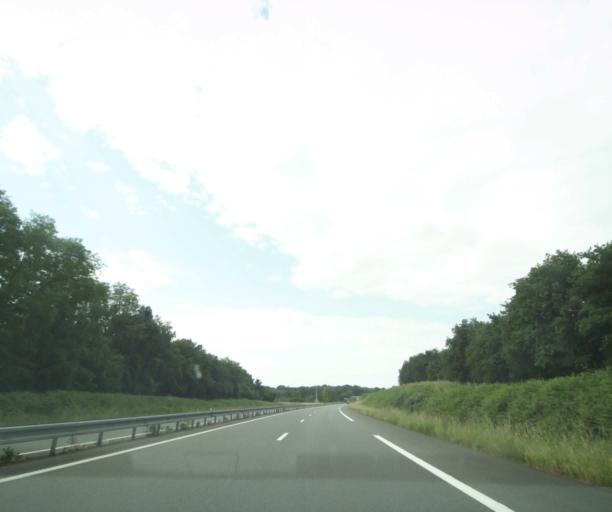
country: FR
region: Pays de la Loire
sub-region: Departement de Maine-et-Loire
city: Brion
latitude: 47.4388
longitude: -0.1730
